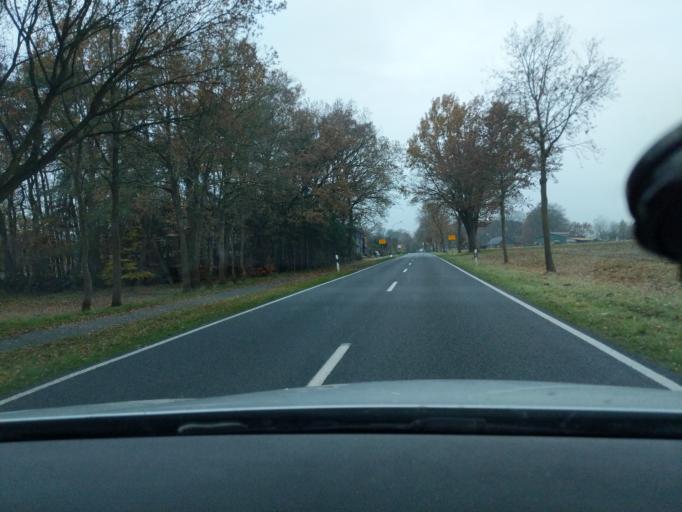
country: DE
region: Lower Saxony
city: Heeslingen
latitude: 53.3392
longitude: 9.3802
